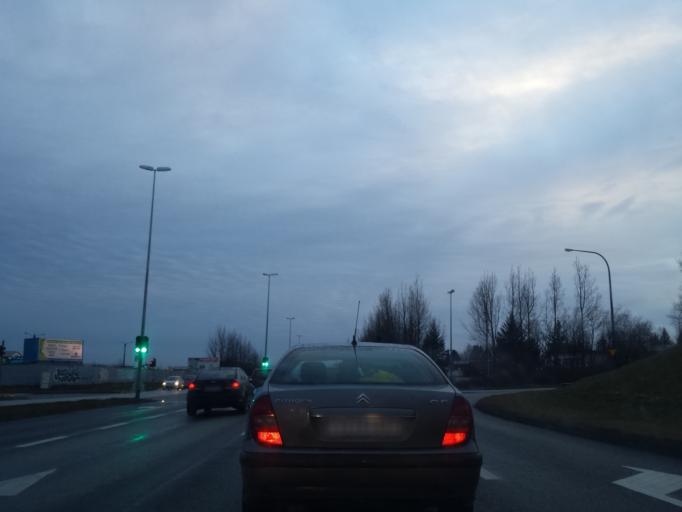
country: IS
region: Capital Region
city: Reykjavik
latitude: 64.1347
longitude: -21.8502
